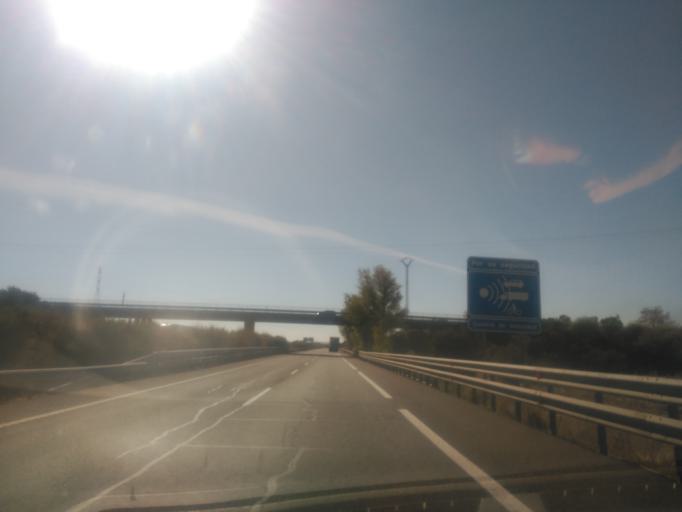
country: ES
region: Castille and Leon
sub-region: Provincia de Valladolid
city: Tordesillas
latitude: 41.5045
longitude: -5.0213
